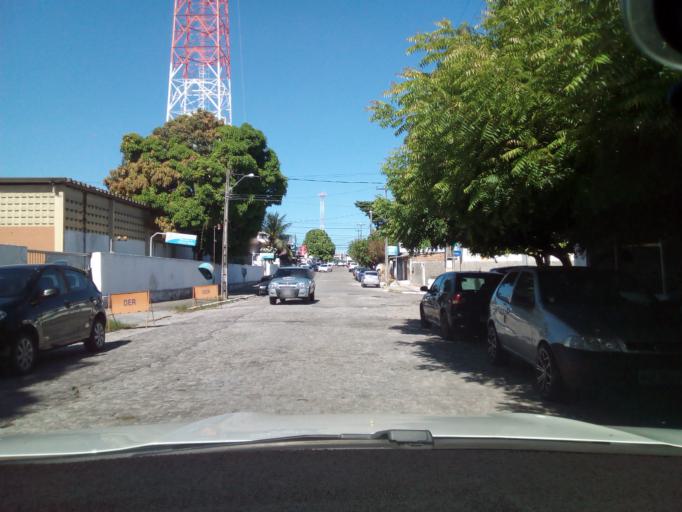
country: BR
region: Paraiba
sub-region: Joao Pessoa
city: Joao Pessoa
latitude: -7.1240
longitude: -34.8714
